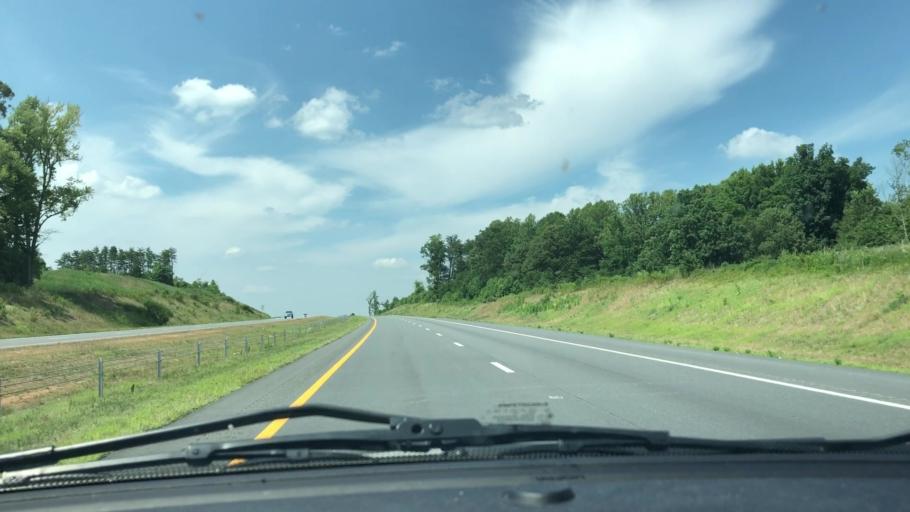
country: US
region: North Carolina
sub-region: Guilford County
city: Summerfield
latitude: 36.1909
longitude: -79.9293
